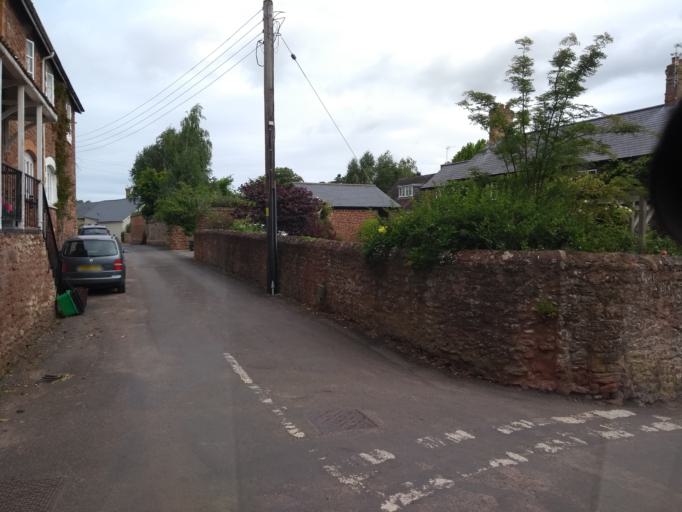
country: GB
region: England
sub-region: Somerset
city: Bishops Lydeard
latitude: 51.0461
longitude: -3.2279
